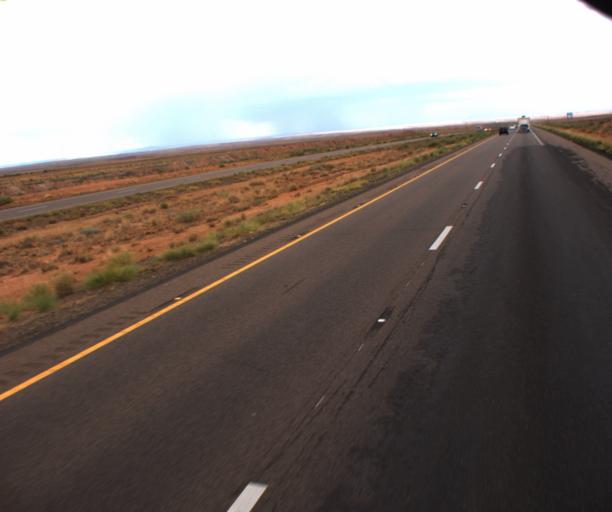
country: US
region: Arizona
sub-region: Coconino County
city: LeChee
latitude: 35.0760
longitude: -110.8640
